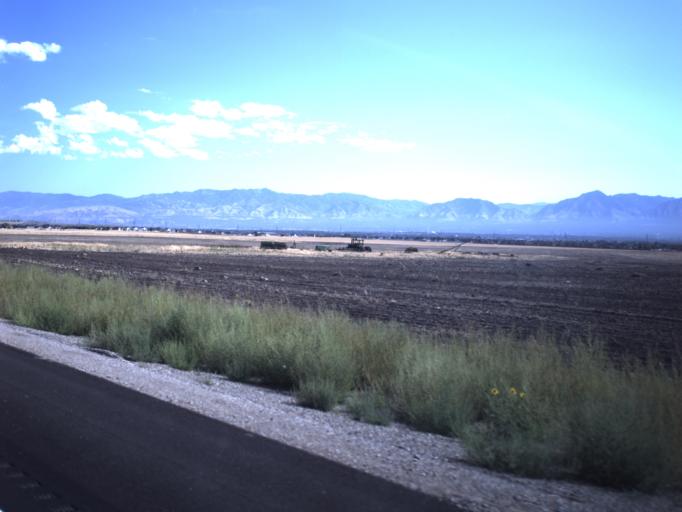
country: US
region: Utah
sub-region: Salt Lake County
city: Oquirrh
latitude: 40.5823
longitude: -112.0605
